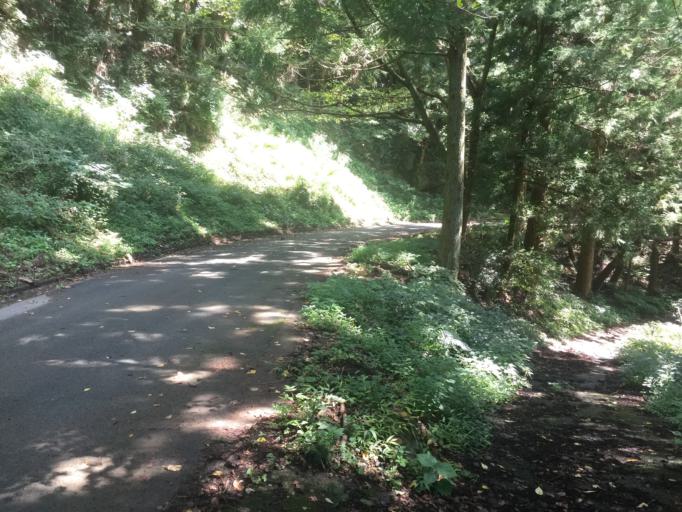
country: JP
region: Shizuoka
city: Kanaya
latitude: 34.8480
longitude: 138.0629
